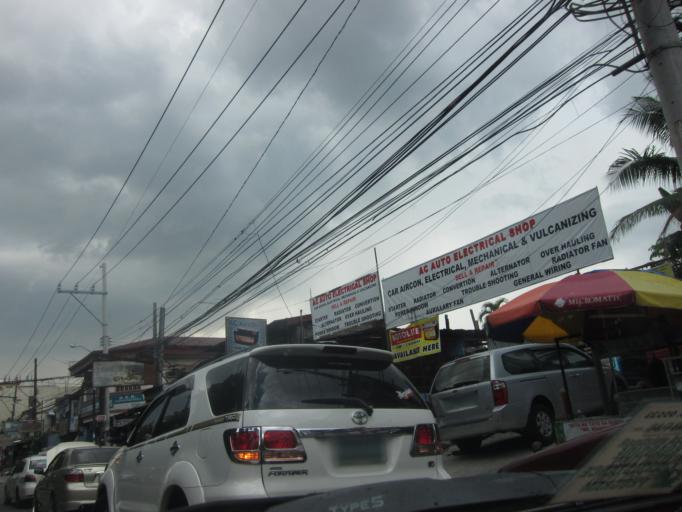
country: PH
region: Metro Manila
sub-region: Quezon City
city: Quezon City
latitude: 14.6367
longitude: 121.0524
